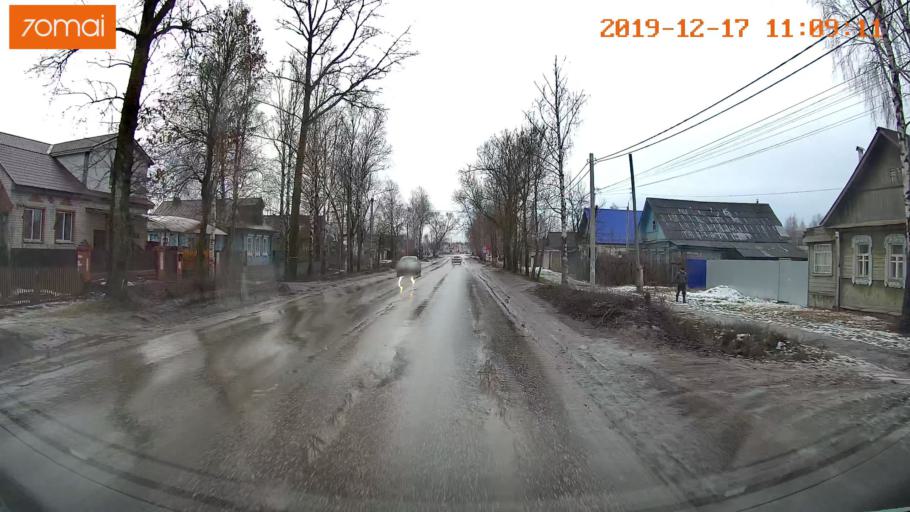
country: RU
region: Vladimir
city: Gus'-Khrustal'nyy
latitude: 55.6025
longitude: 40.6427
